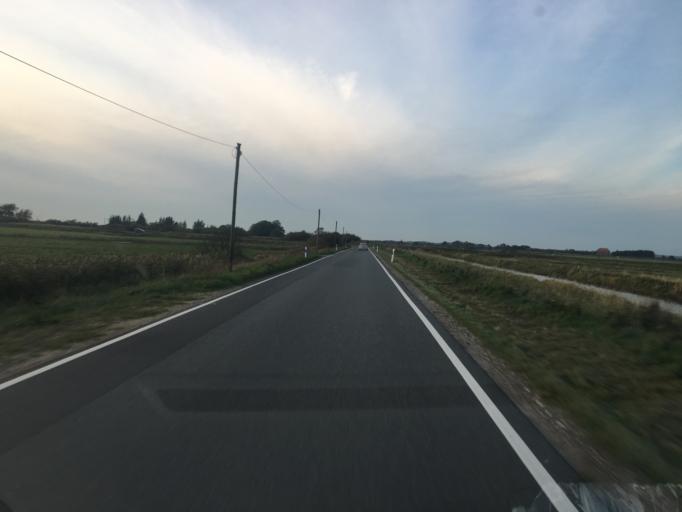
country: DE
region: Schleswig-Holstein
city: Aventoft
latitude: 54.9033
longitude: 8.8393
